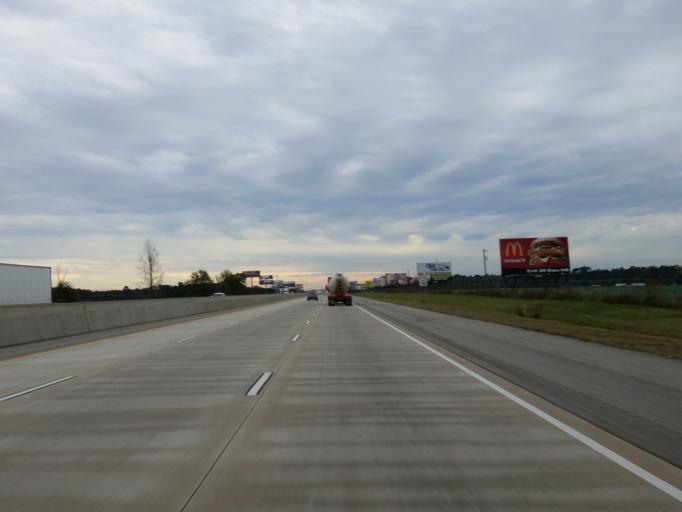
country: US
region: Georgia
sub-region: Cook County
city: Sparks
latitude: 31.1831
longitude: -83.4534
